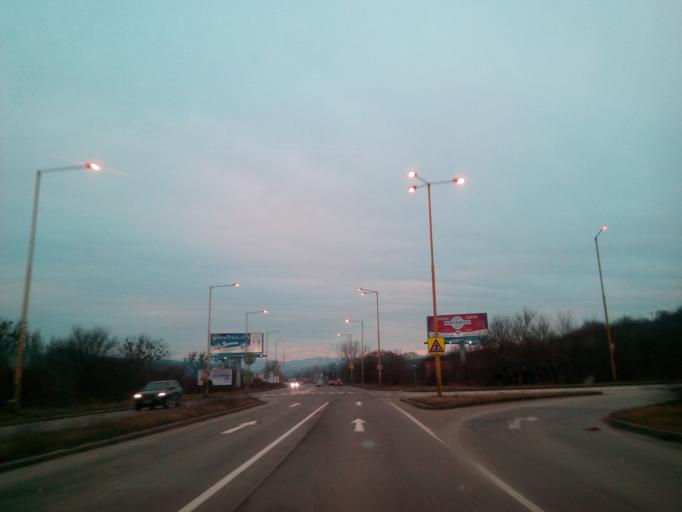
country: SK
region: Kosicky
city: Kosice
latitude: 48.6979
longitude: 21.2270
